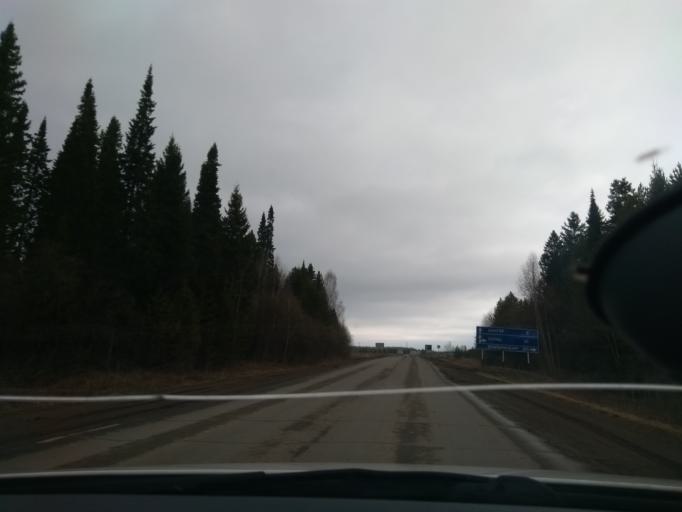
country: RU
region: Perm
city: Kungur
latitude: 57.3985
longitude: 56.8798
